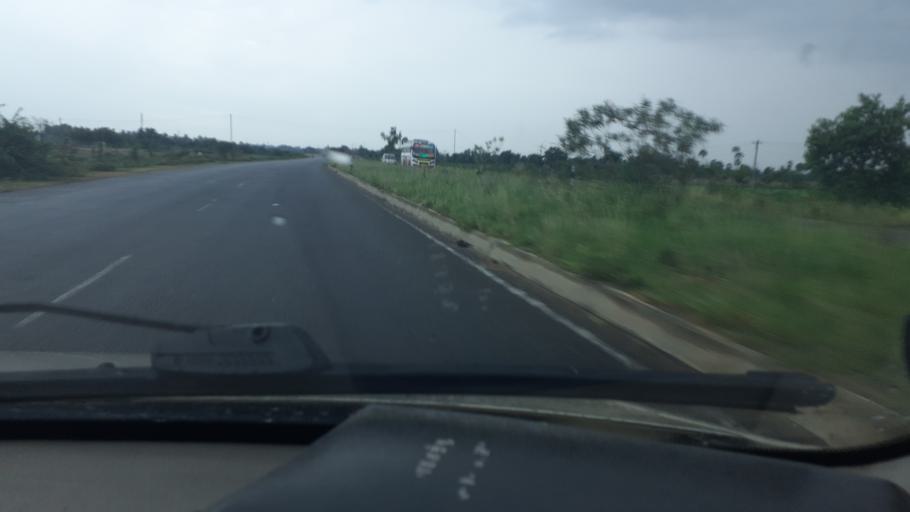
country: IN
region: Tamil Nadu
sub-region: Thoothukkudi
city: Kadambur
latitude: 9.0573
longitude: 77.7971
